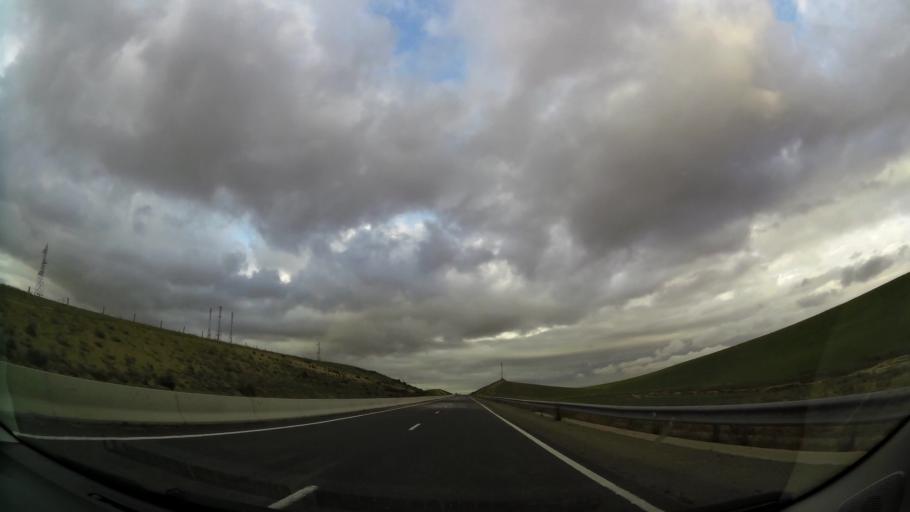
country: MA
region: Taza-Al Hoceima-Taounate
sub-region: Taza
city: Taza
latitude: 34.2681
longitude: -3.8326
